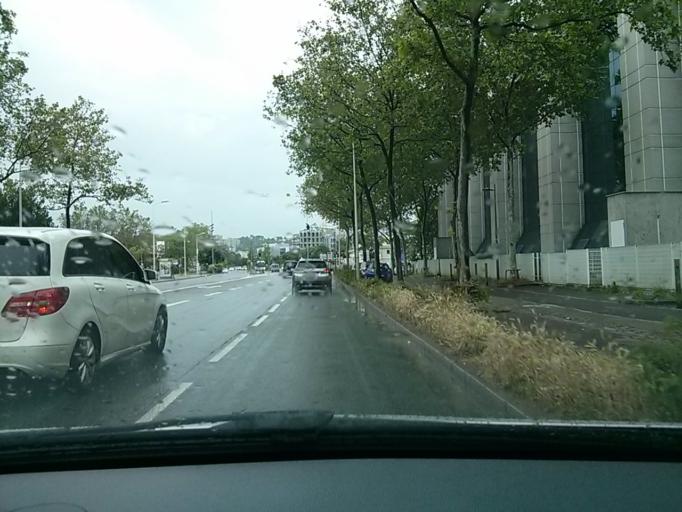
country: FR
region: Rhone-Alpes
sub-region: Departement du Rhone
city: La Mulatiere
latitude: 45.7266
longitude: 4.8329
